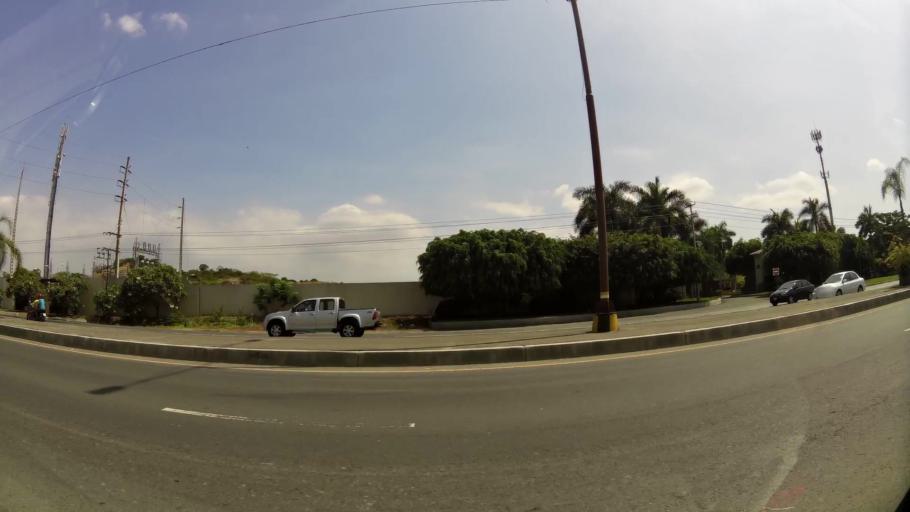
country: EC
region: Guayas
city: Eloy Alfaro
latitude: -2.0786
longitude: -79.8737
